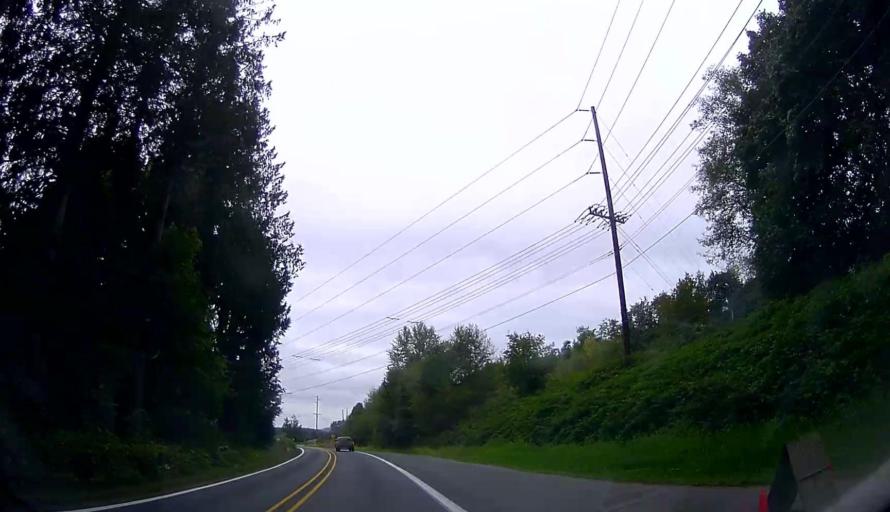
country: US
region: Washington
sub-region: Snohomish County
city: Warm Beach
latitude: 48.2019
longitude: -122.3376
